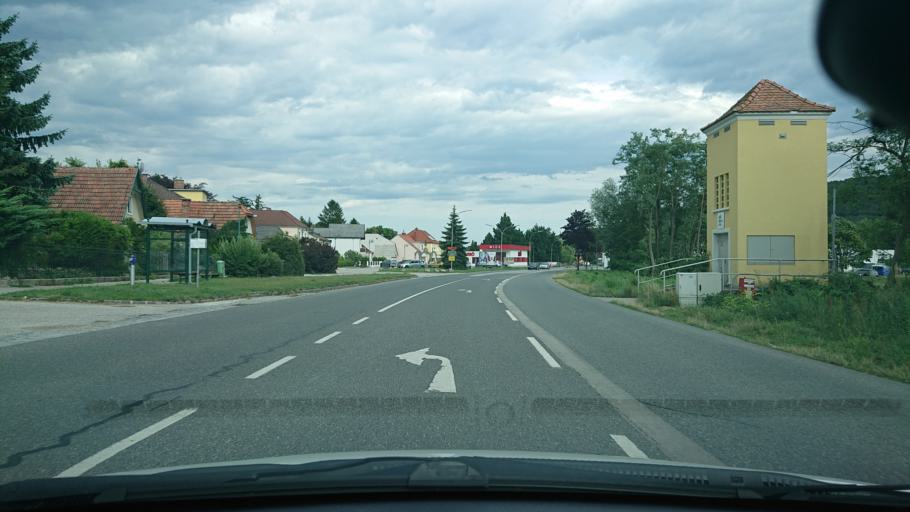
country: AT
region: Lower Austria
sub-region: Politischer Bezirk Baden
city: Berndorf
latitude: 47.9392
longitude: 16.1433
